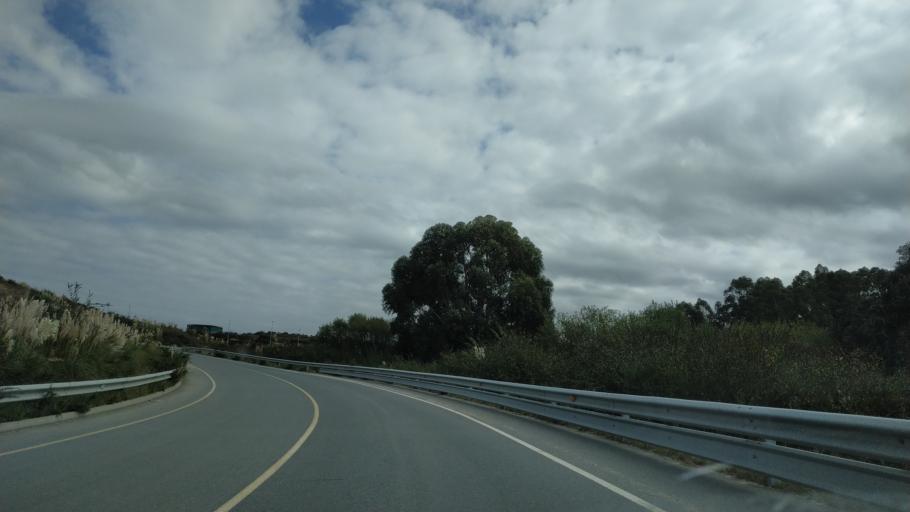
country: ES
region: Galicia
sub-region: Provincia da Coruna
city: Arteixo
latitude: 43.3287
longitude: -8.4582
